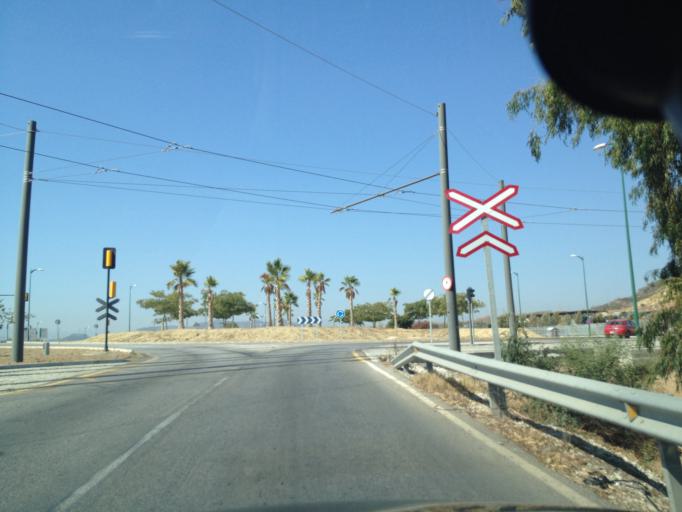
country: ES
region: Andalusia
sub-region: Provincia de Malaga
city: Alhaurin de la Torre
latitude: 36.7195
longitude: -4.5051
